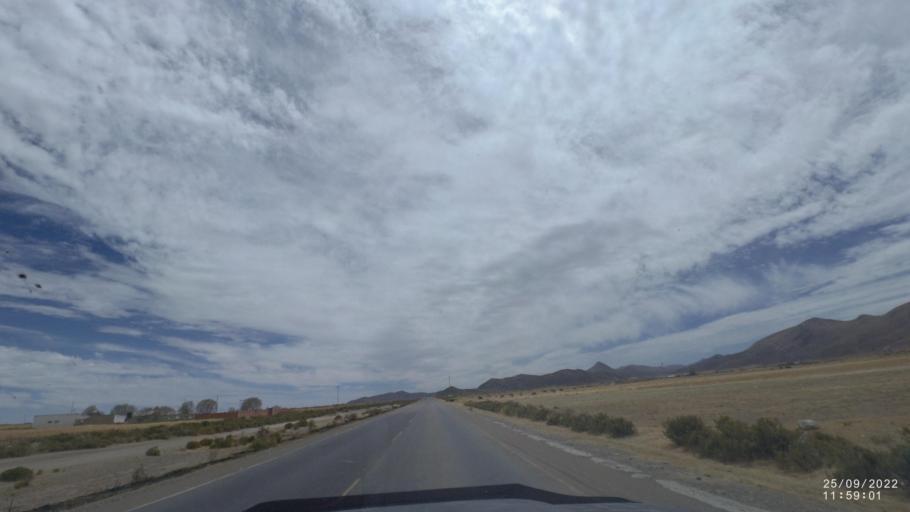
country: BO
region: Oruro
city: Challapata
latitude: -18.7942
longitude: -66.8432
